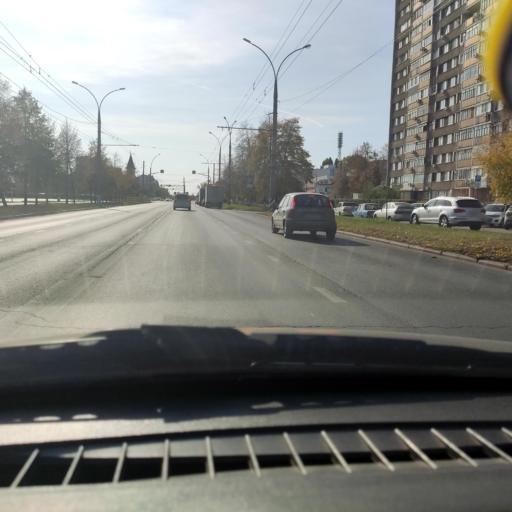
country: RU
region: Samara
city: Tol'yatti
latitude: 53.5087
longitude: 49.2712
